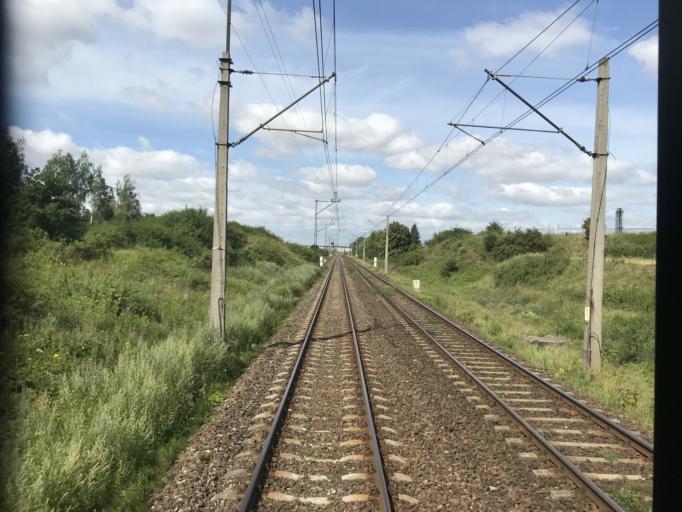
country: PL
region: Pomeranian Voivodeship
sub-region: Powiat malborski
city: Malbork
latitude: 54.0337
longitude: 19.0797
